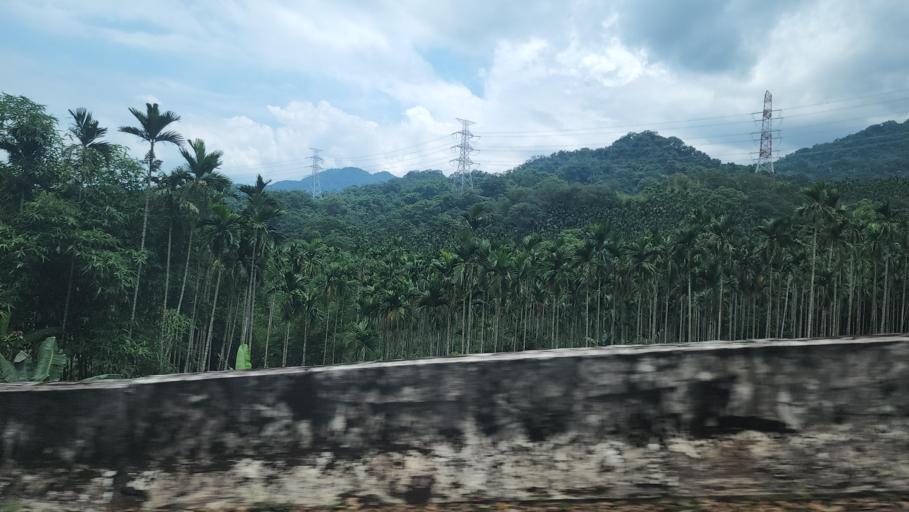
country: TW
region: Taipei
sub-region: Taipei
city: Banqiao
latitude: 24.9186
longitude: 121.4197
